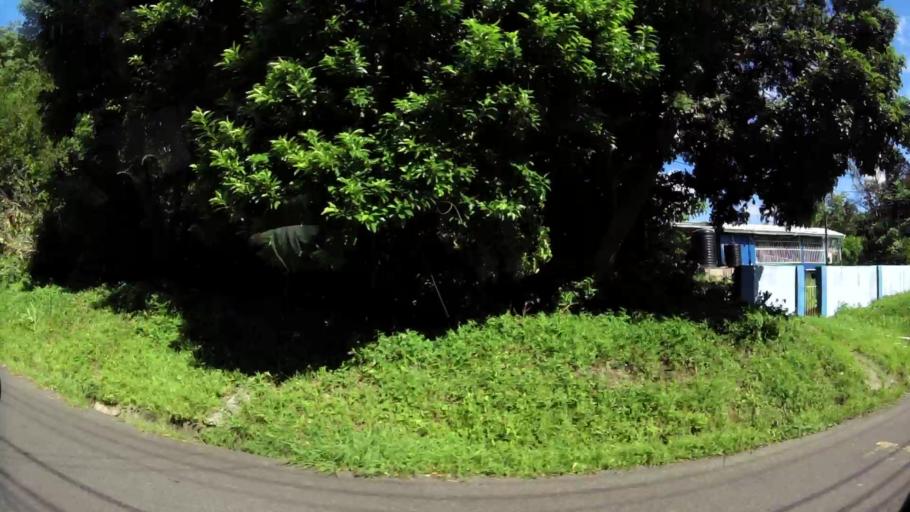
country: TT
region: Tobago
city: Scarborough
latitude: 11.1719
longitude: -60.7210
